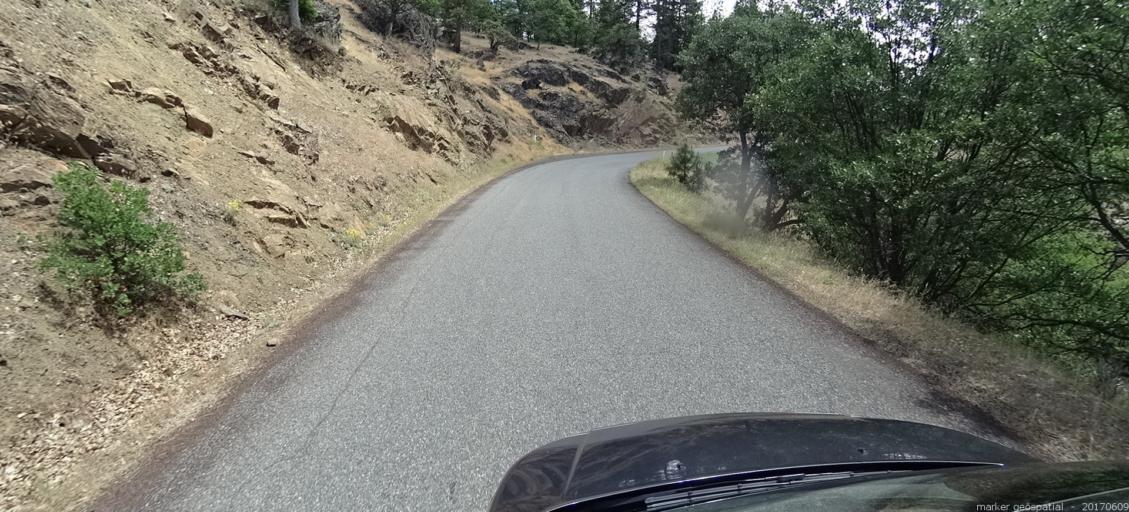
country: US
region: California
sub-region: Siskiyou County
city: Yreka
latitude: 41.3779
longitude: -122.8927
